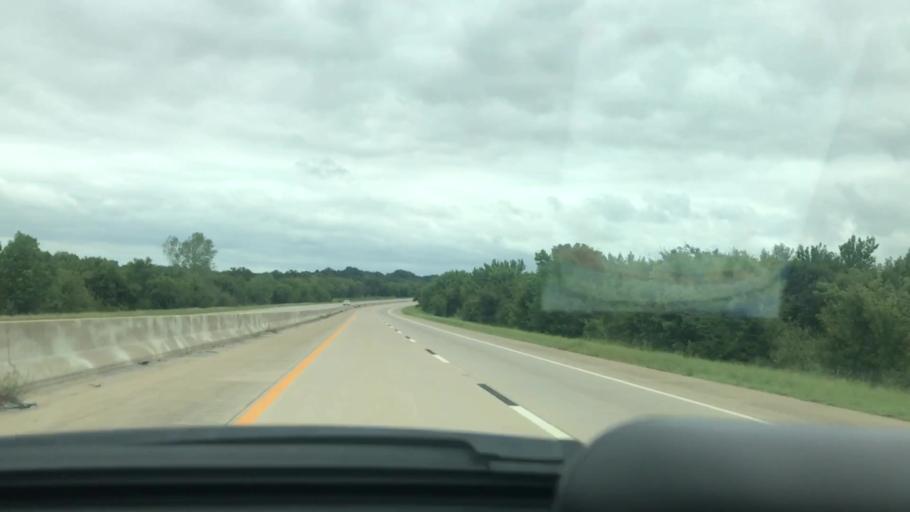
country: US
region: Oklahoma
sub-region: McIntosh County
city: Eufaula
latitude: 35.1890
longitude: -95.6392
